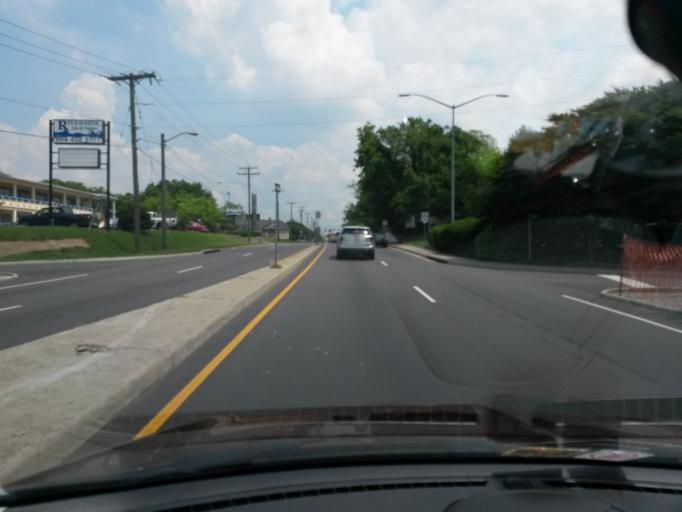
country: US
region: Virginia
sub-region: City of Hopewell
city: Hopewell
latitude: 37.3093
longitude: -77.2955
